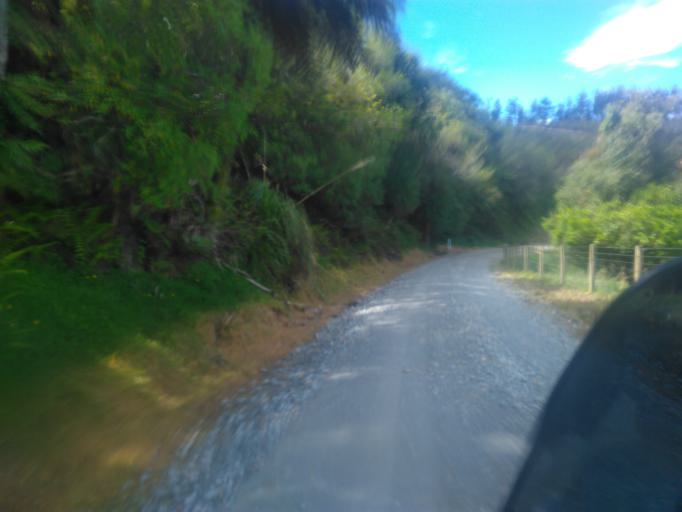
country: NZ
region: Hawke's Bay
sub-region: Wairoa District
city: Wairoa
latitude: -38.7763
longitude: 177.6250
